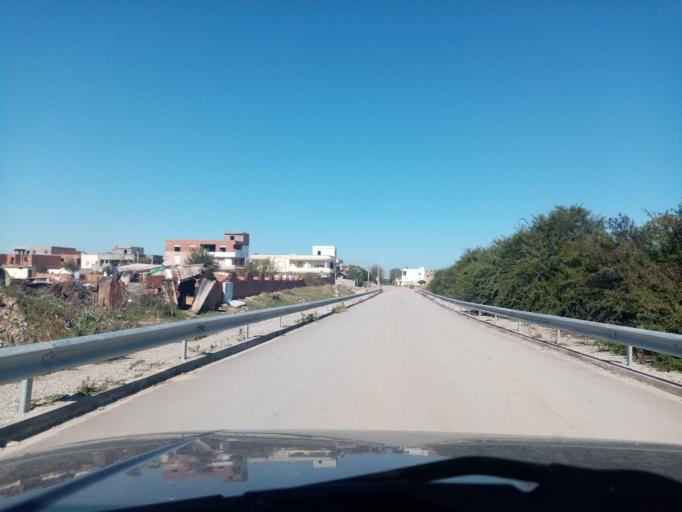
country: TN
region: Nabul
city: Bu `Urqub
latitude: 36.5801
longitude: 10.5701
